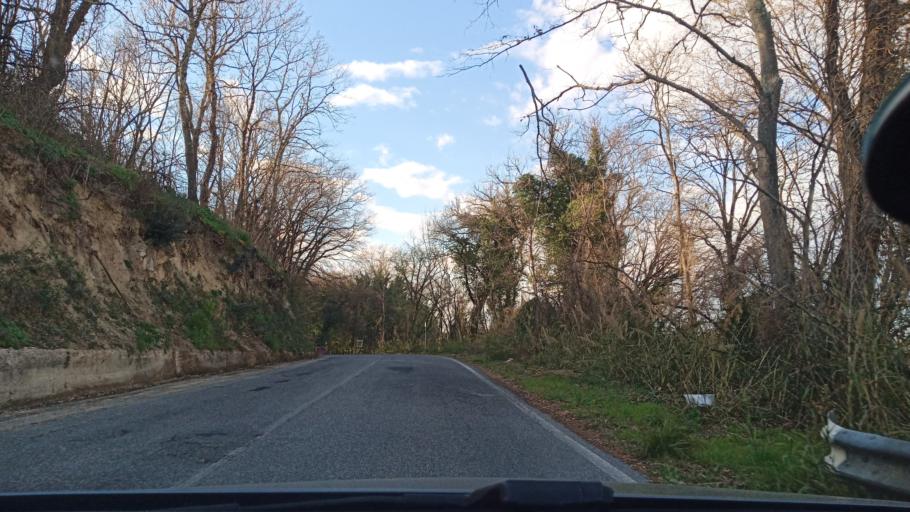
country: IT
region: Latium
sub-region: Citta metropolitana di Roma Capitale
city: Nazzano
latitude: 42.2071
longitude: 12.6053
